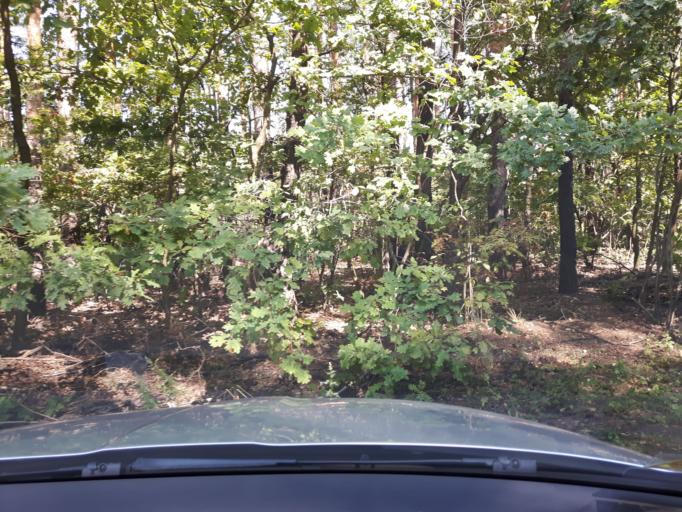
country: PL
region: Masovian Voivodeship
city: Zielonka
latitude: 52.2891
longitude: 21.1559
